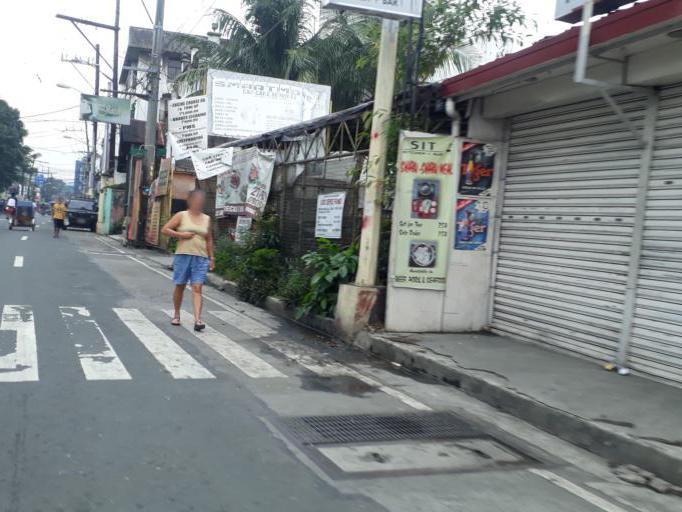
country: PH
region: Metro Manila
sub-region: Caloocan City
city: Niugan
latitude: 14.6556
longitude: 120.9720
